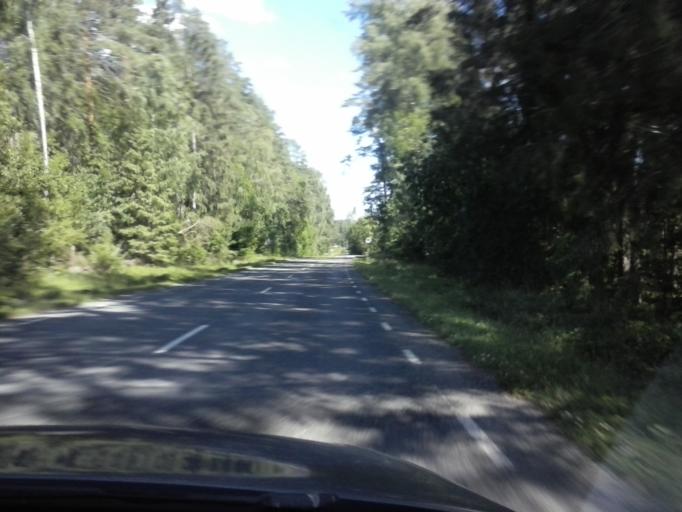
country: EE
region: Vorumaa
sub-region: Voru linn
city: Voru
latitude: 57.7255
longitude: 26.9009
